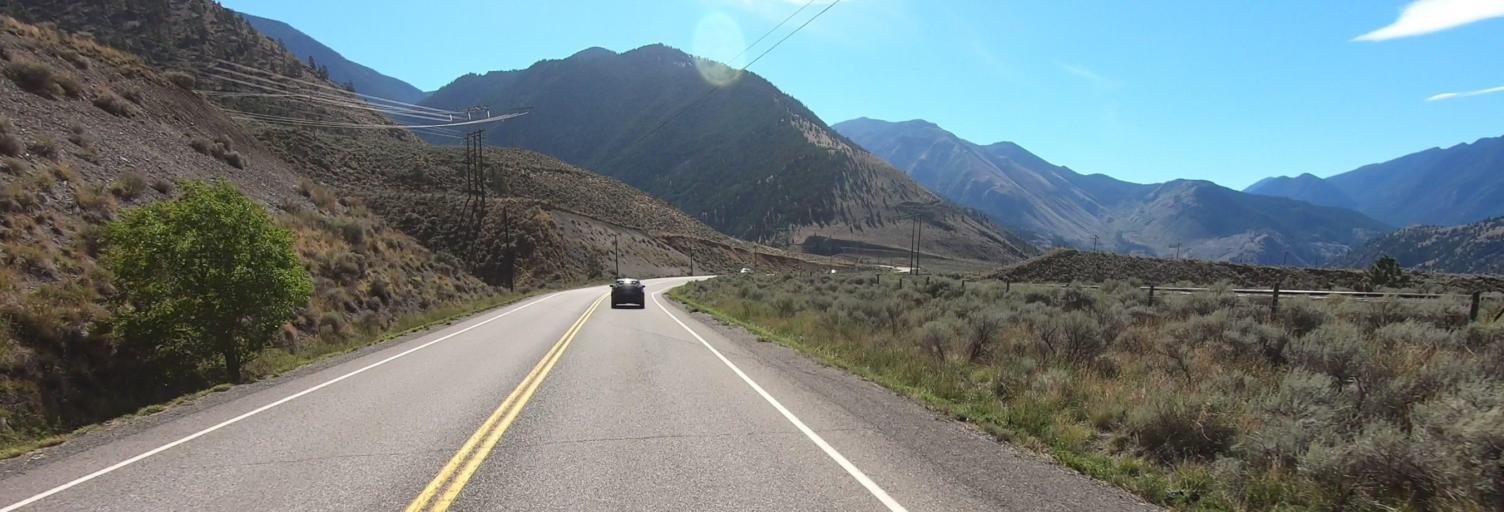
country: CA
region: British Columbia
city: Lillooet
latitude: 50.8023
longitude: -121.8472
